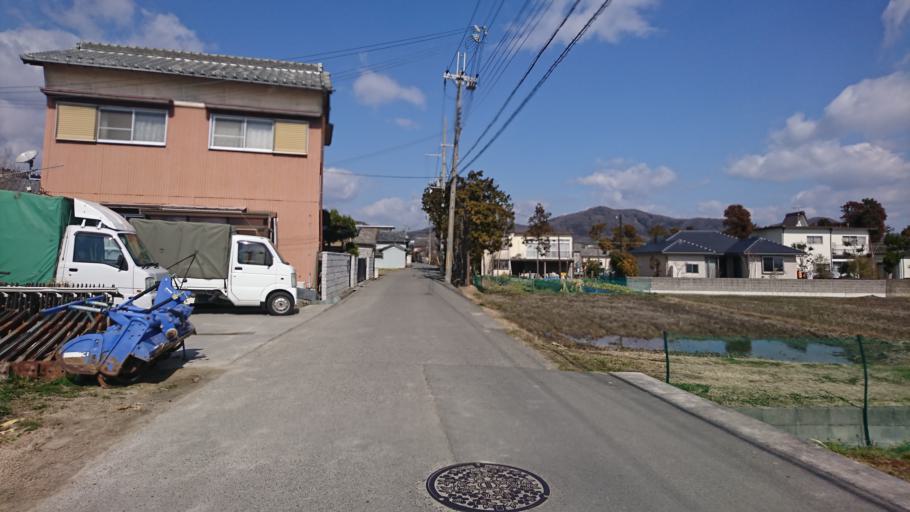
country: JP
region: Hyogo
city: Kakogawacho-honmachi
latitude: 34.8116
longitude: 134.8048
